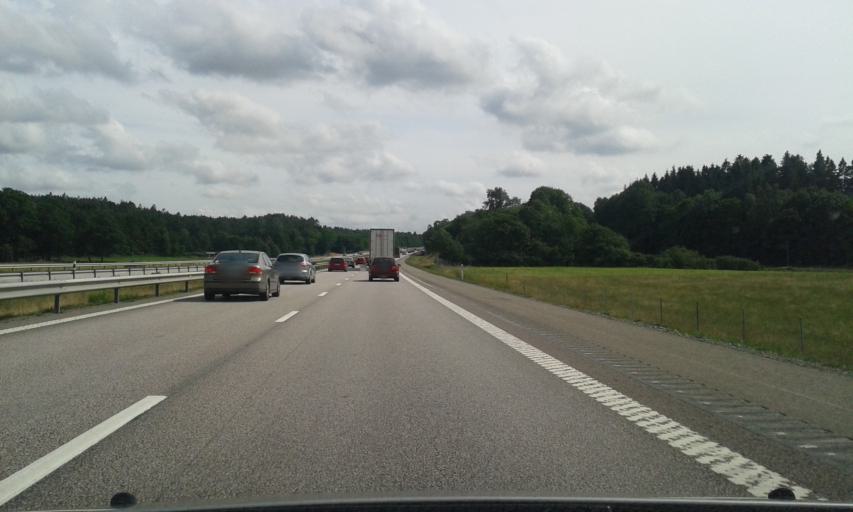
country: SE
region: Halland
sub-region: Kungsbacka Kommun
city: Frillesas
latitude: 57.3651
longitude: 12.2057
